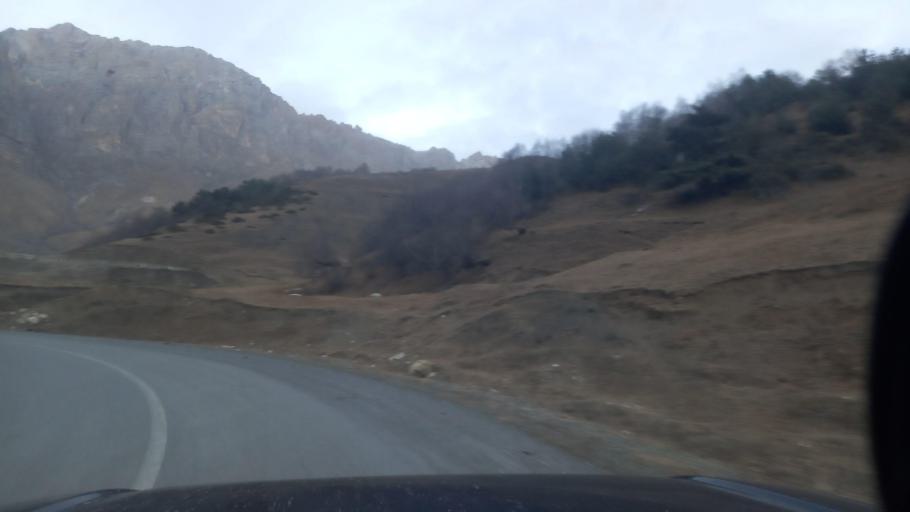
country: RU
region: Ingushetiya
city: Dzhayrakh
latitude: 42.8175
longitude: 44.8152
